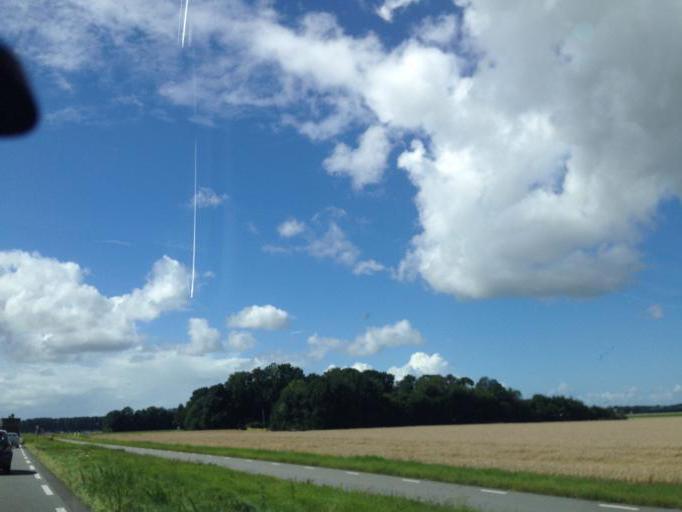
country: NL
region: Flevoland
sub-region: Gemeente Dronten
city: Dronten
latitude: 52.5372
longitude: 5.7594
